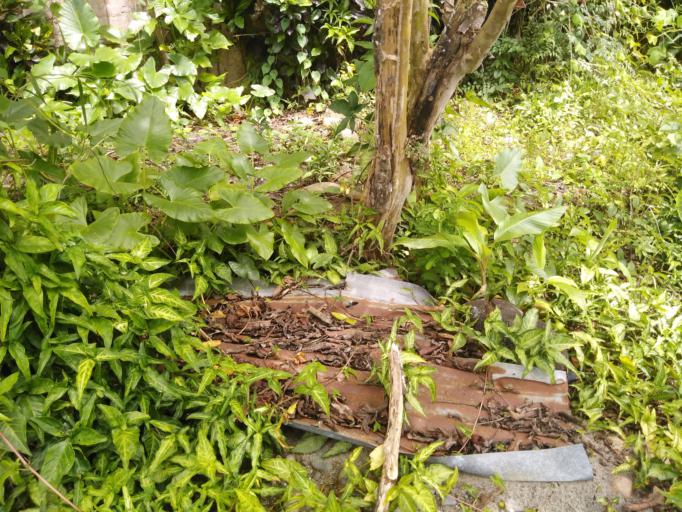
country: EC
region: Napo
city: Tena
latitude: -1.0604
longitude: -77.5459
